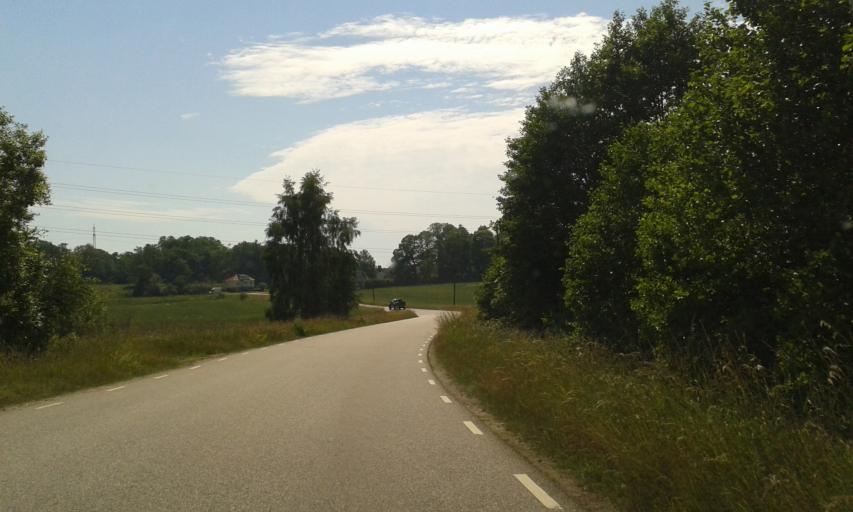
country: SE
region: Blekinge
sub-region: Karlskrona Kommun
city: Rodeby
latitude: 56.2273
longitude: 15.5853
